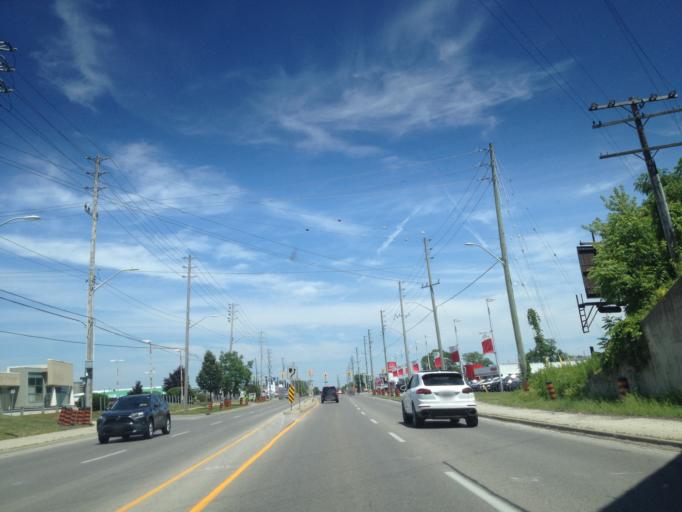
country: CA
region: Ontario
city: London
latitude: 42.9822
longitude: -81.2980
